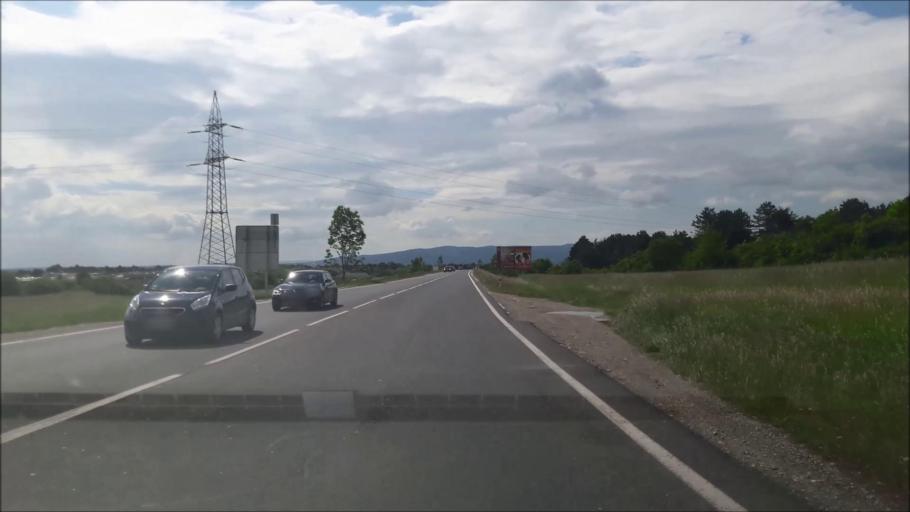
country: AT
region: Lower Austria
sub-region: Politischer Bezirk Wiener Neustadt
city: Theresienfeld
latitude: 47.8553
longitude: 16.1885
